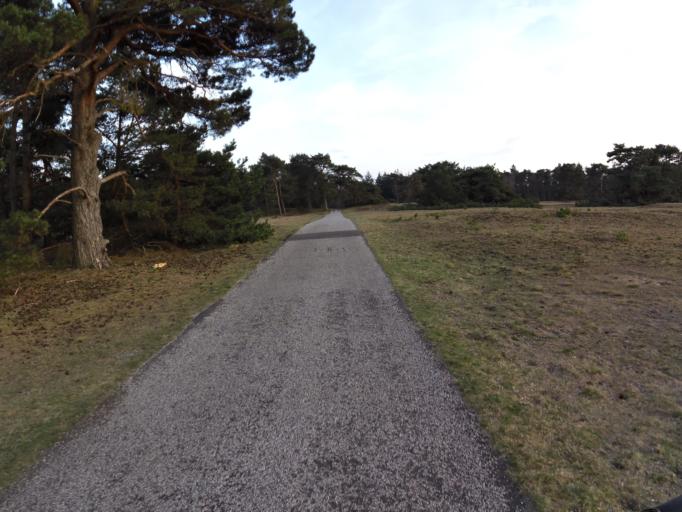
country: NL
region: Gelderland
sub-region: Gemeente Ede
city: Otterlo
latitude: 52.1020
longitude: 5.8027
